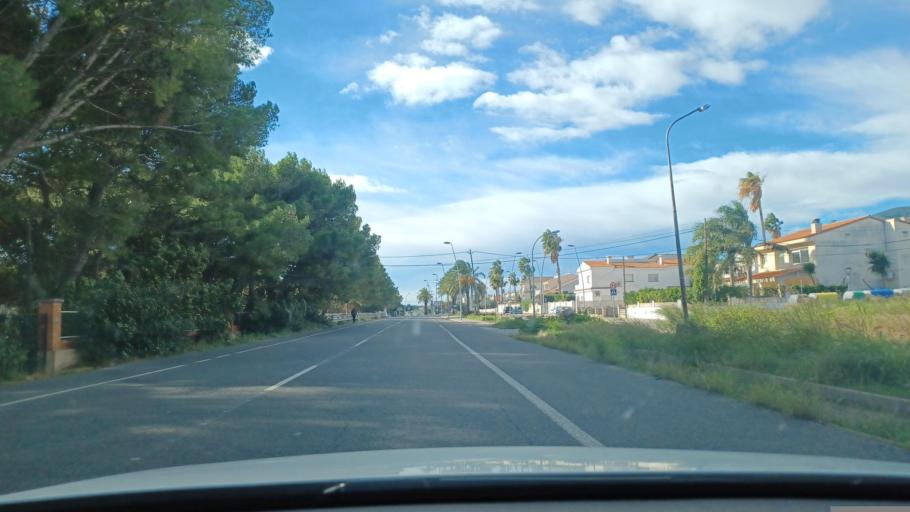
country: ES
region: Catalonia
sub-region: Provincia de Tarragona
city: Sant Carles de la Rapita
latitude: 40.5971
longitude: 0.5719
